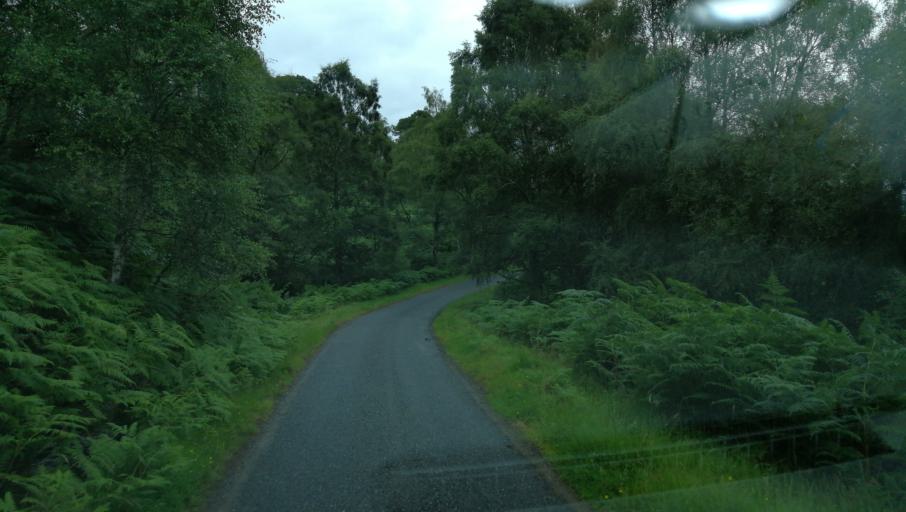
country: GB
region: Scotland
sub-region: Highland
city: Spean Bridge
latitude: 57.2869
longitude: -4.9213
